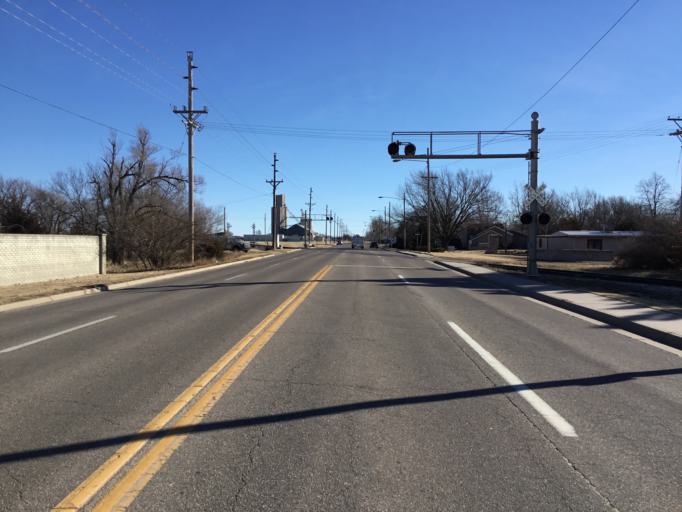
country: US
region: Kansas
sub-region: McPherson County
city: McPherson
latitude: 38.3767
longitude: -97.6447
